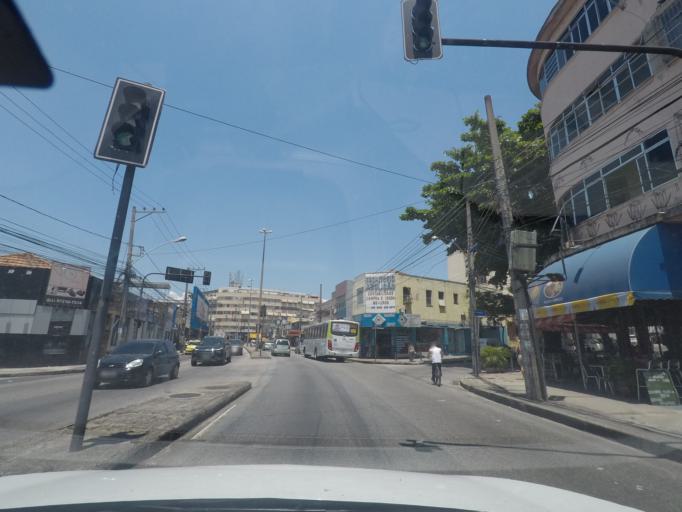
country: BR
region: Rio de Janeiro
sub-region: Rio De Janeiro
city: Rio de Janeiro
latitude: -22.8854
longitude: -43.2997
